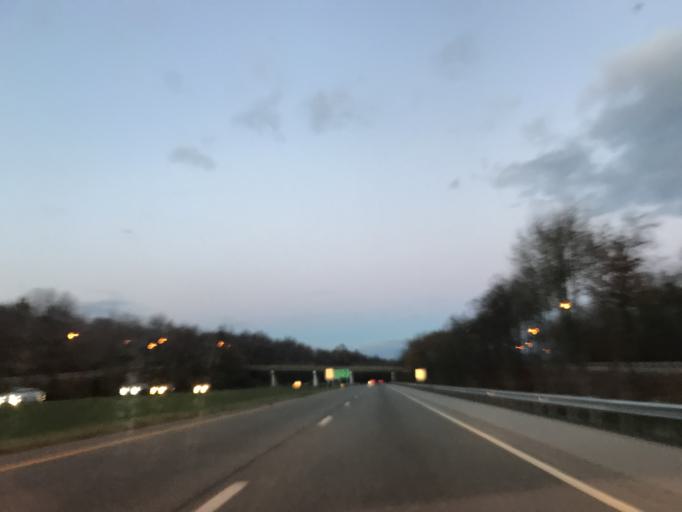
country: US
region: Delaware
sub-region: New Castle County
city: Claymont
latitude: 39.8013
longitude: -75.4822
